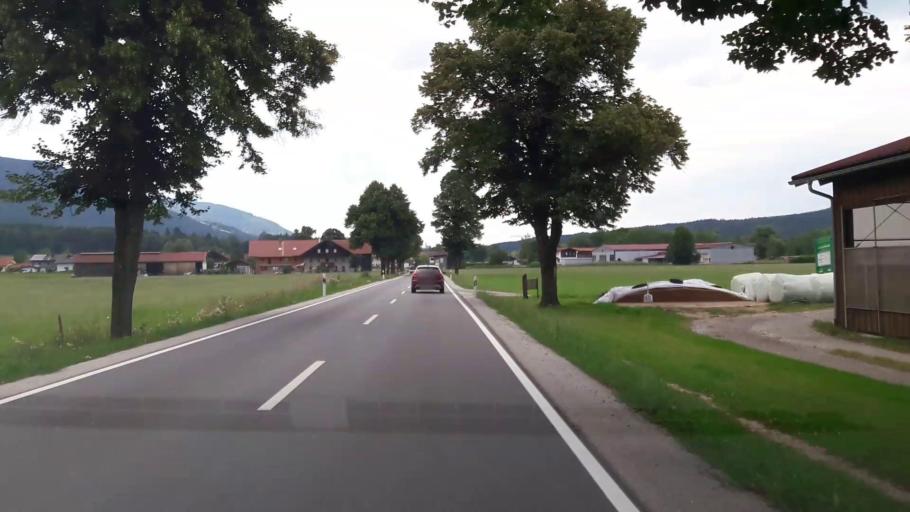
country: DE
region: Bavaria
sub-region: Upper Bavaria
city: Piding
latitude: 47.7648
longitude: 12.8974
